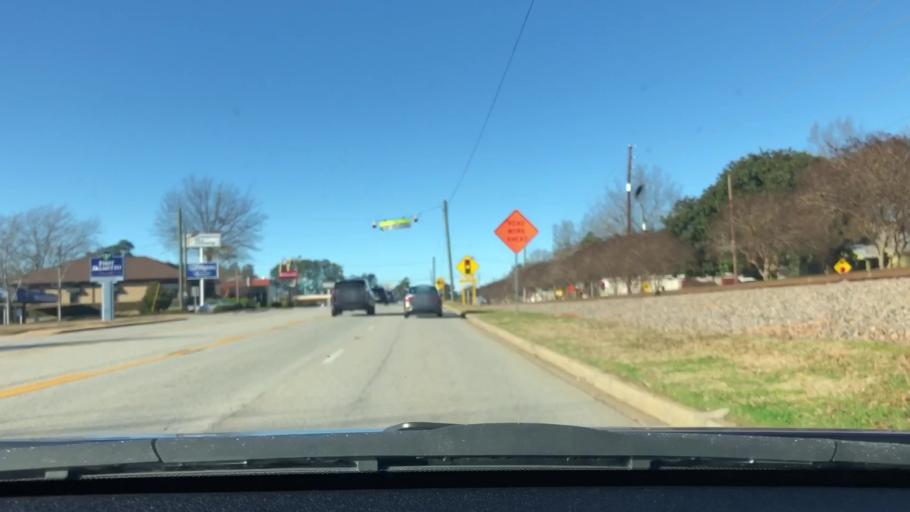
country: US
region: South Carolina
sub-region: Lexington County
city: Irmo
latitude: 34.0839
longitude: -81.1823
